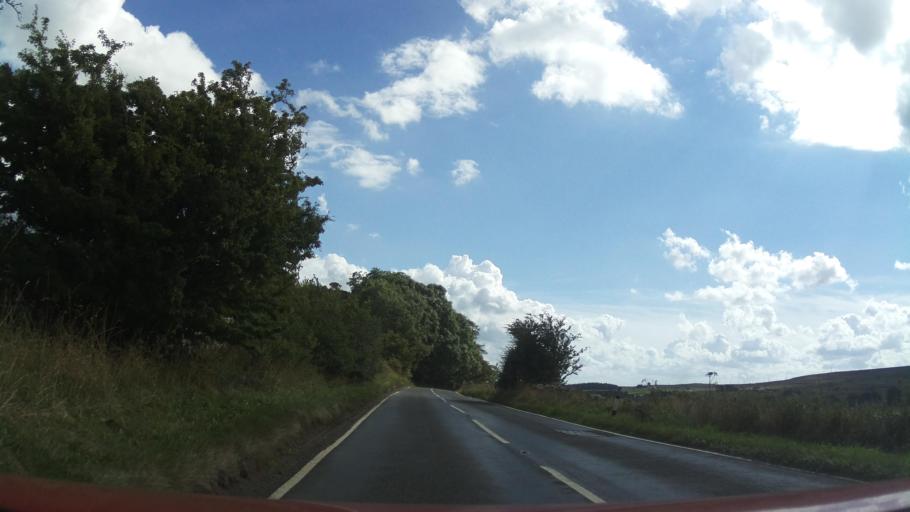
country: GB
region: England
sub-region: North Yorkshire
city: Leyburn
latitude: 54.3700
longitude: -1.8273
